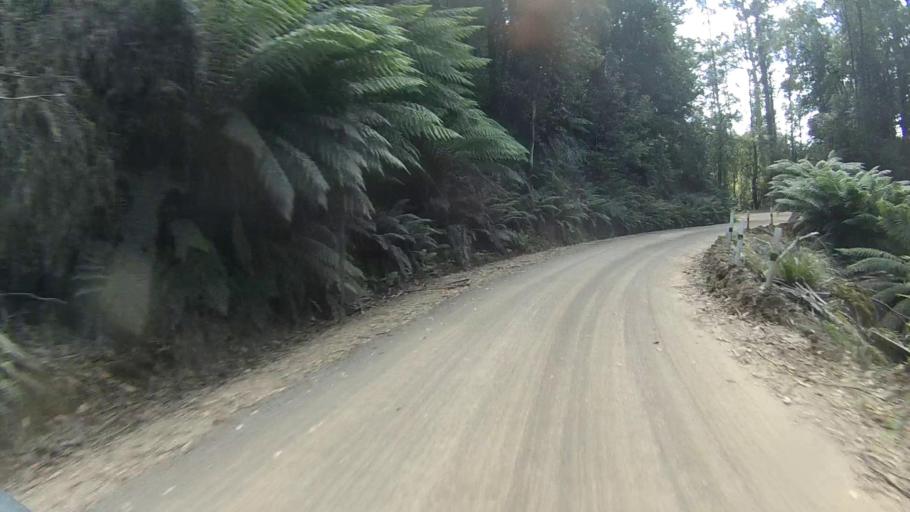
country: AU
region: Tasmania
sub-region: Derwent Valley
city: New Norfolk
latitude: -42.6796
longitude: 146.6879
